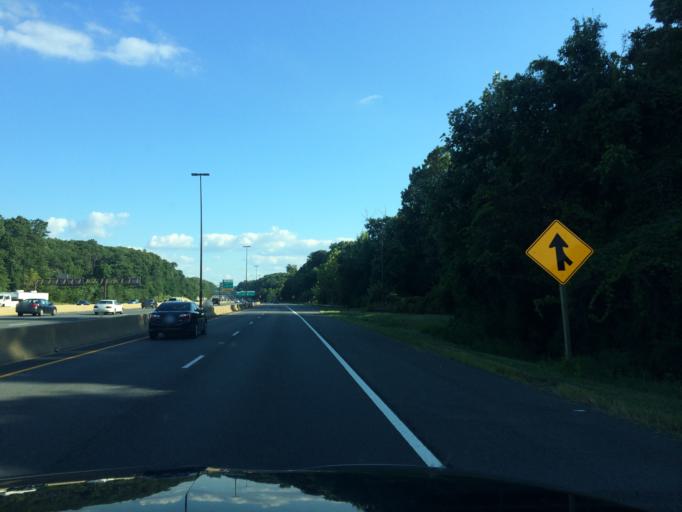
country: US
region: Maryland
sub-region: Montgomery County
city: Rockville
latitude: 39.0546
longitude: -77.1541
